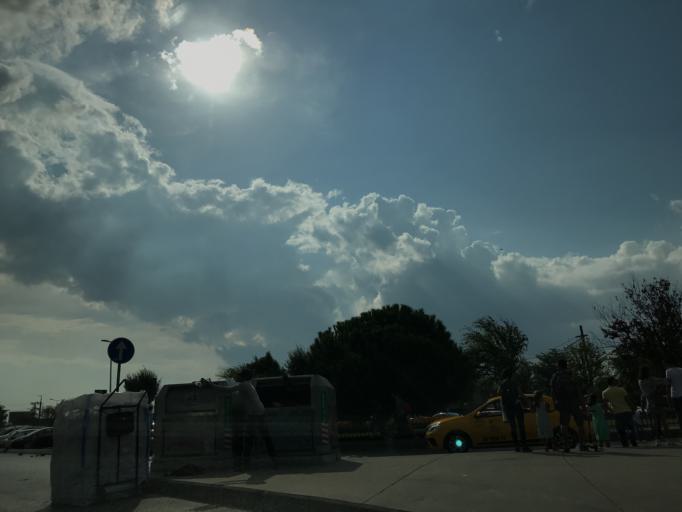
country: TR
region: Istanbul
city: UEskuedar
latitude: 40.9894
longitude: 29.0216
